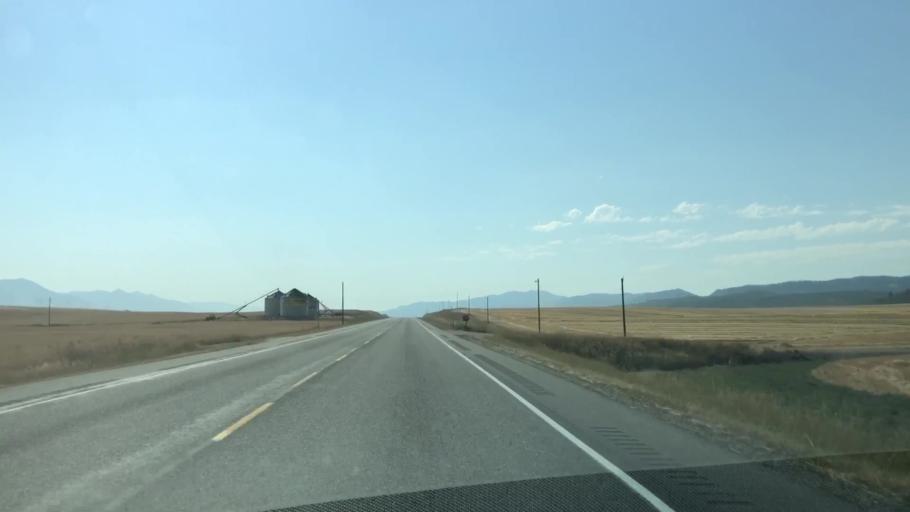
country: US
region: Idaho
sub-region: Teton County
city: Victor
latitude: 43.5177
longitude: -111.4876
